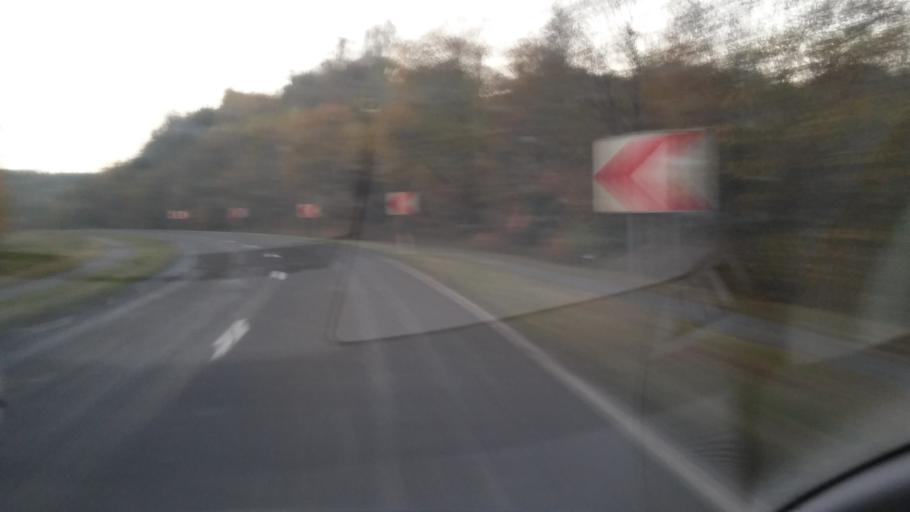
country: BE
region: Wallonia
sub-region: Province du Luxembourg
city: Etalle
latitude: 49.6424
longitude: 5.5689
